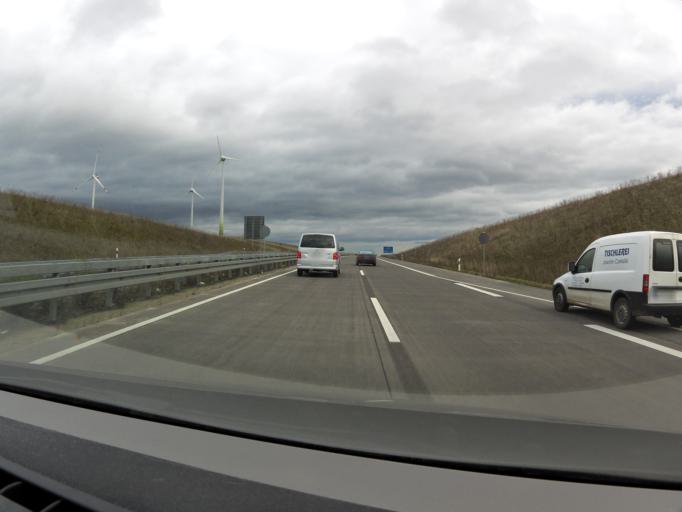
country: DE
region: Thuringia
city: Artern
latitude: 51.3854
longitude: 11.2787
